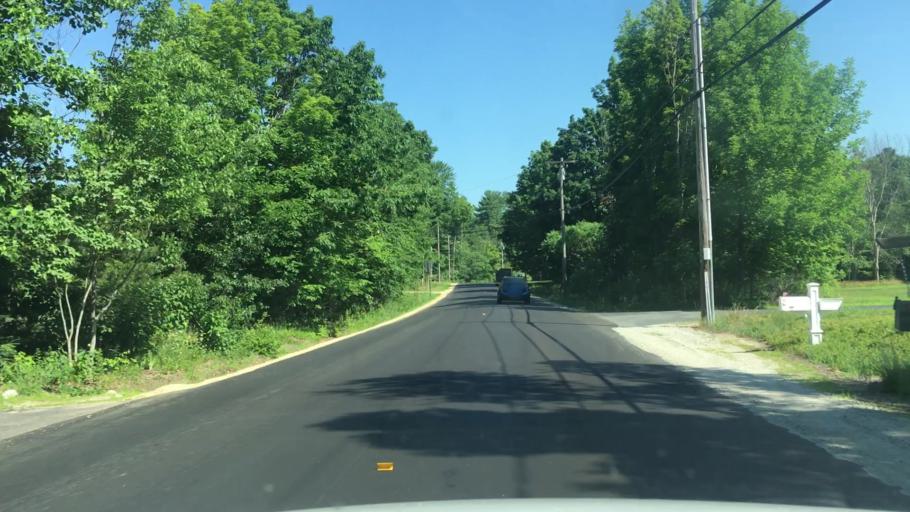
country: US
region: Maine
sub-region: Cumberland County
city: Cumberland Center
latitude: 43.8002
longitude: -70.3285
